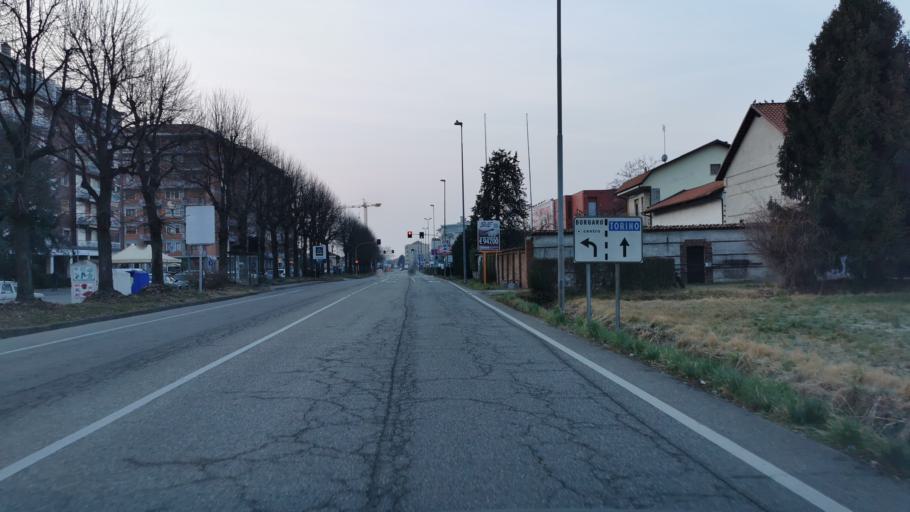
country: IT
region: Piedmont
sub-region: Provincia di Torino
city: Borgaro Torinese
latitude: 45.1566
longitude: 7.6548
